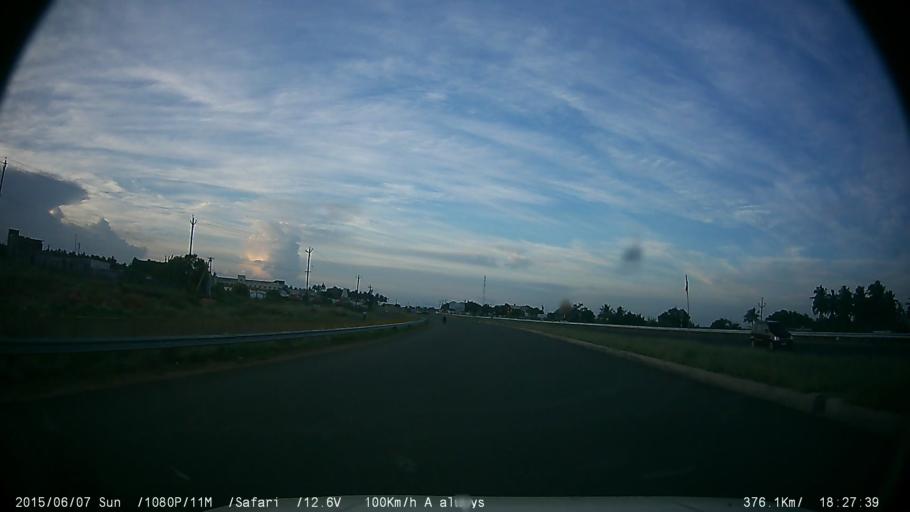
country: IN
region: Tamil Nadu
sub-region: Tiruppur
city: Avinashi
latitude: 11.1376
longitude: 77.2028
